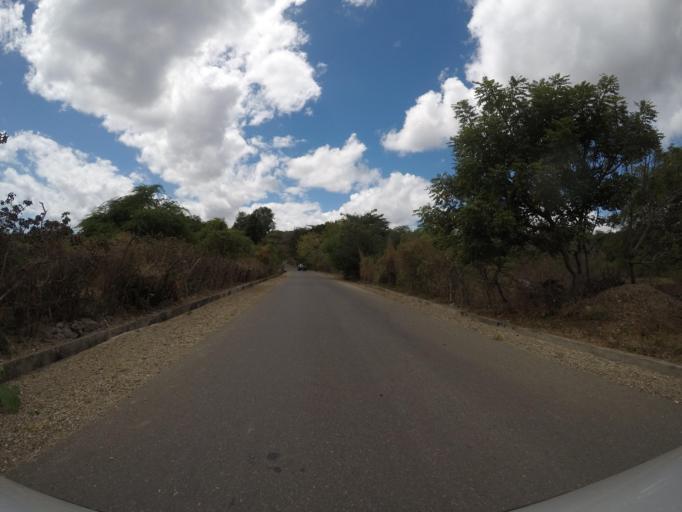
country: TL
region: Lautem
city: Lospalos
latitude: -8.3520
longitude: 126.9199
